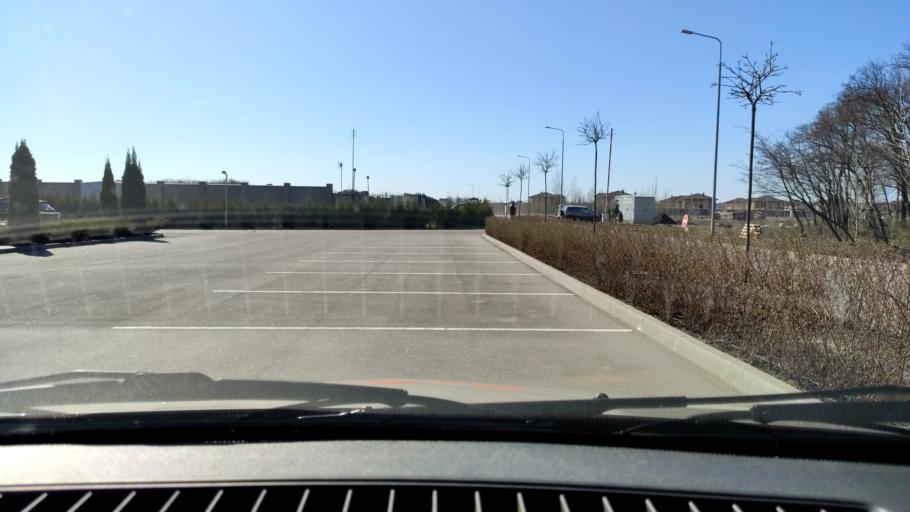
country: RU
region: Voronezj
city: Somovo
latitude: 51.6870
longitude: 39.3392
